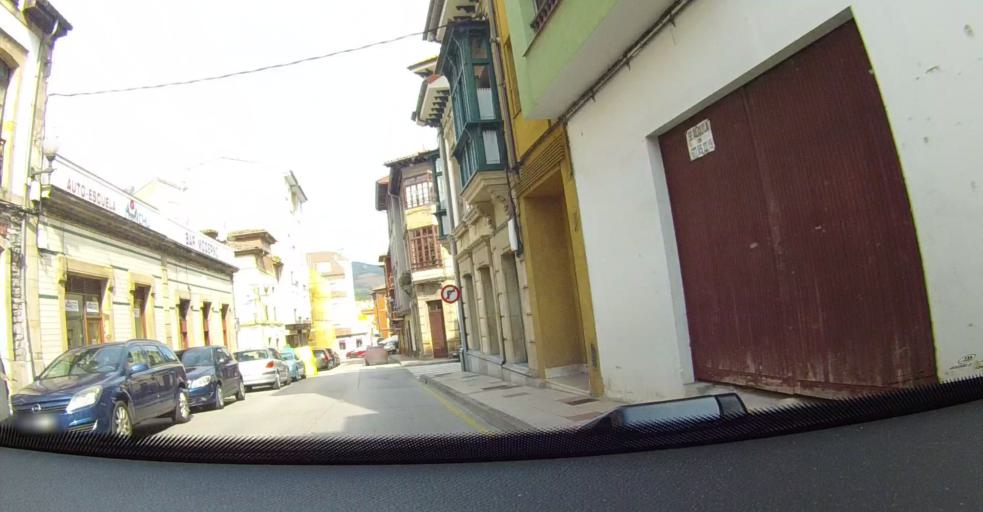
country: ES
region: Asturias
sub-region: Province of Asturias
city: Villaviciosa
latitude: 43.4796
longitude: -5.4342
